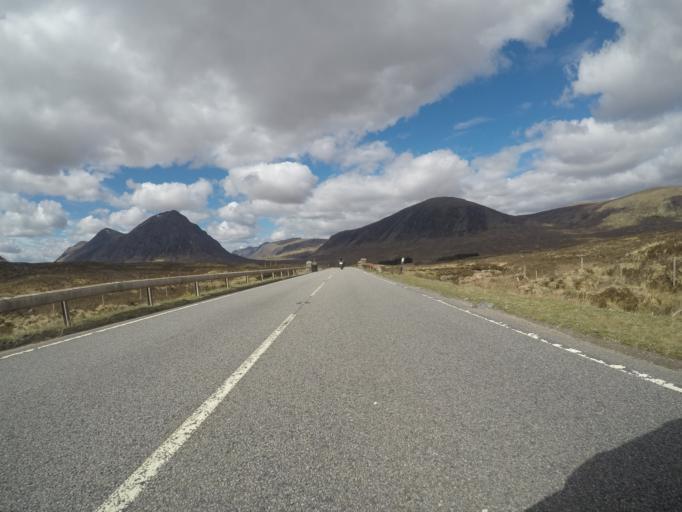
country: GB
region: Scotland
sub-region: Highland
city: Spean Bridge
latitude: 56.6448
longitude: -4.8315
